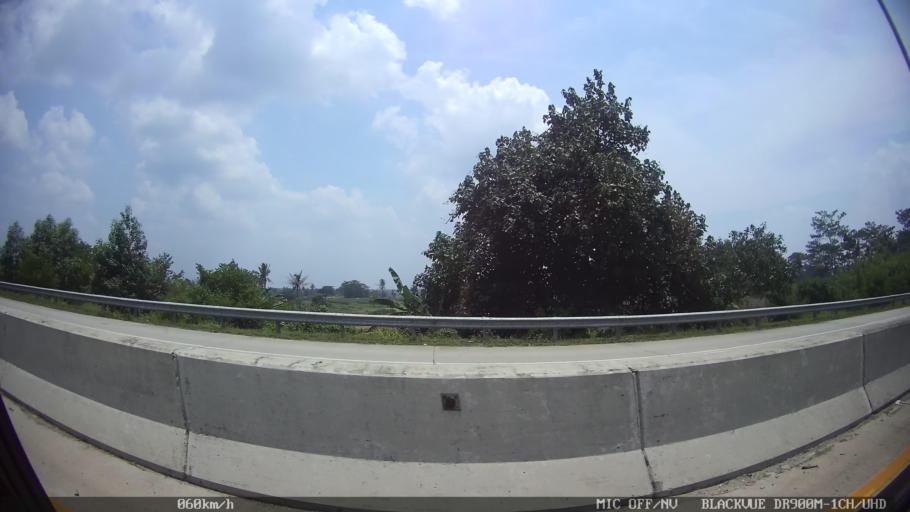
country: ID
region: Lampung
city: Natar
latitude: -5.2814
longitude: 105.1952
